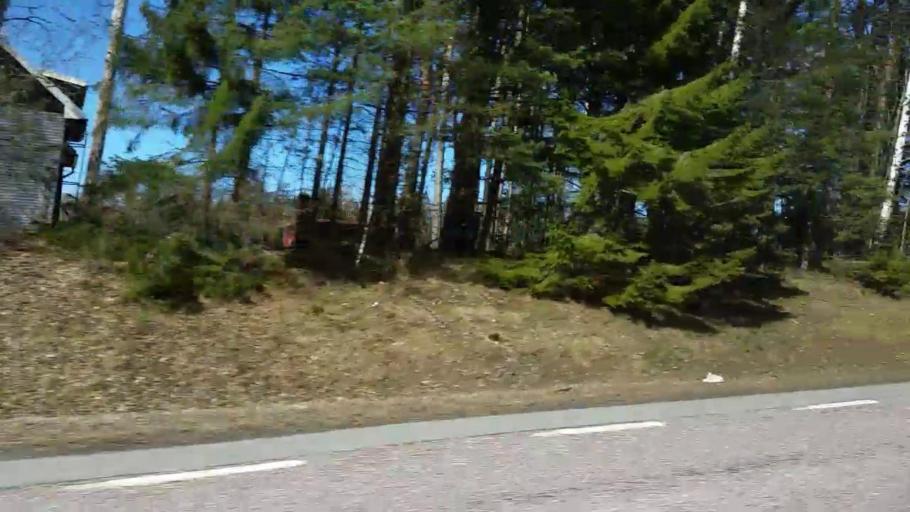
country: SE
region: Gaevleborg
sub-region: Gavle Kommun
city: Norrsundet
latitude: 60.8266
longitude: 17.2118
